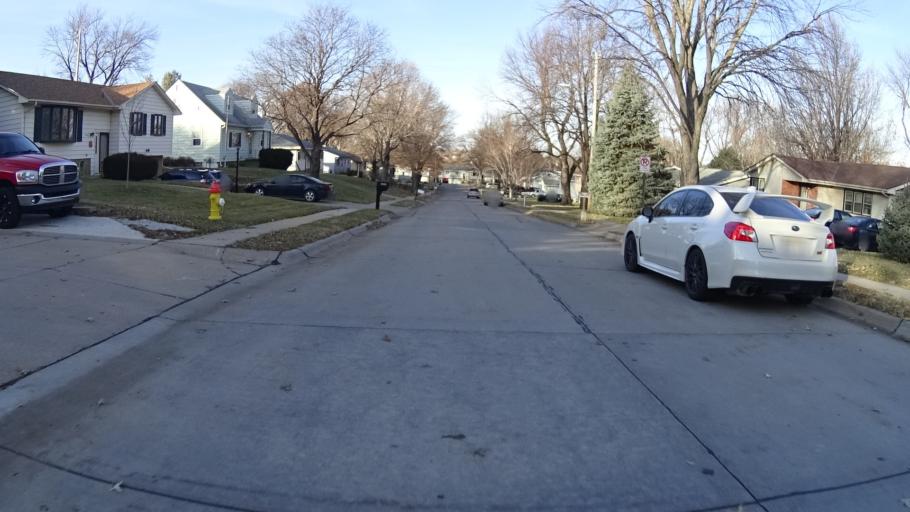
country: US
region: Nebraska
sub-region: Douglas County
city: Ralston
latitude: 41.1924
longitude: -96.0472
